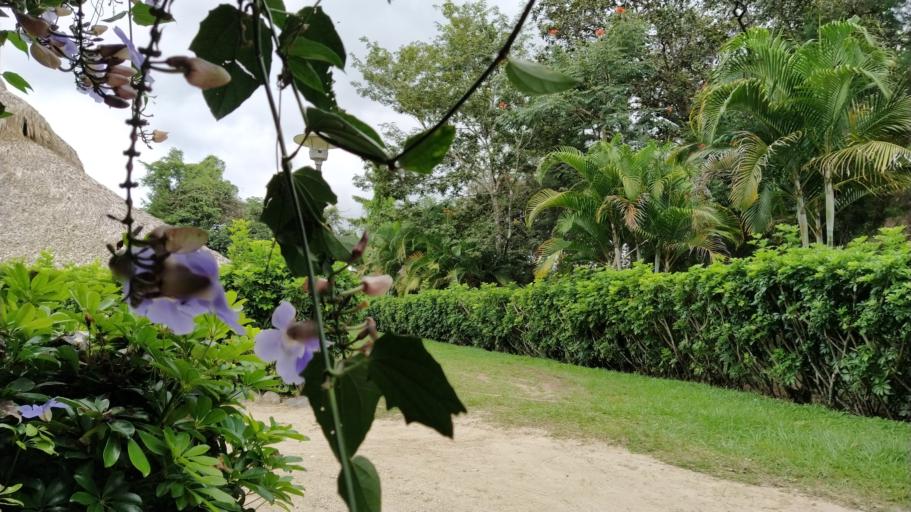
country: GT
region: Chiquimula
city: Esquipulas
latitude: 14.5585
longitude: -89.3169
